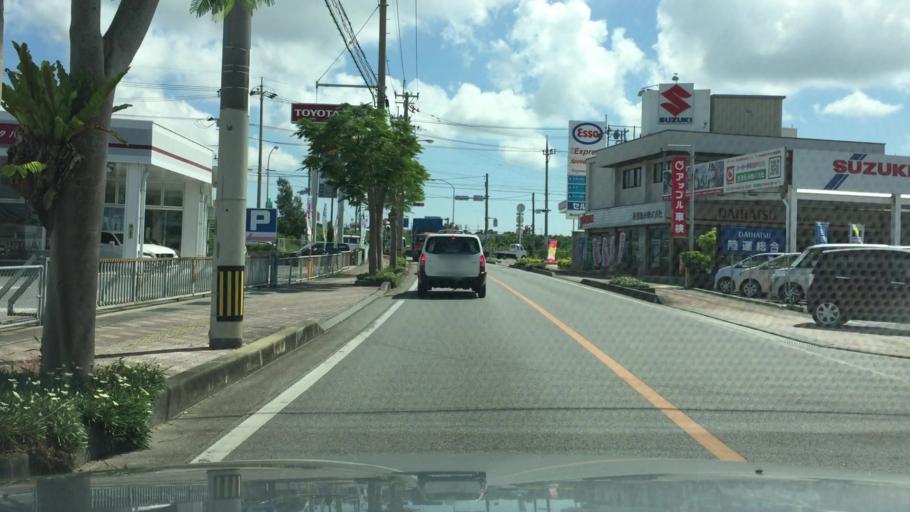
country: JP
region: Okinawa
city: Ishigaki
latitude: 24.3471
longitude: 124.1679
